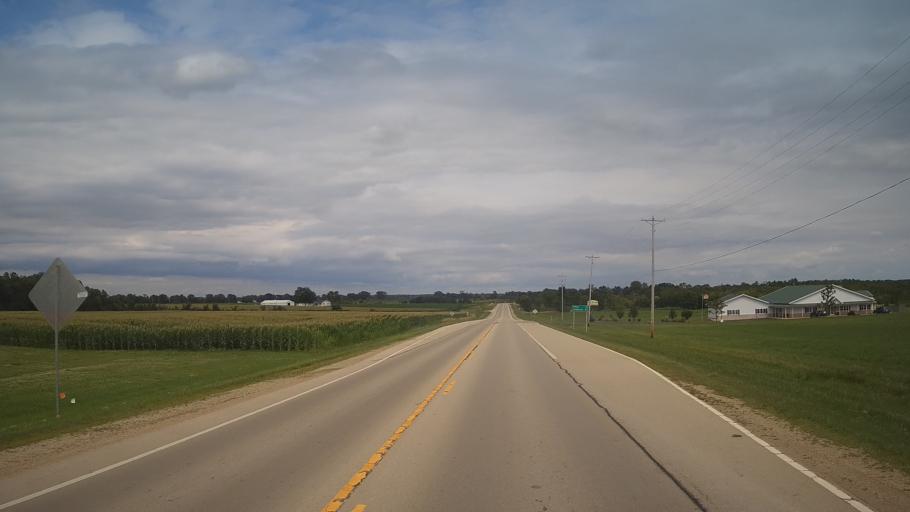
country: US
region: Wisconsin
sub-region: Green Lake County
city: Berlin
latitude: 44.0437
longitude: -88.9818
